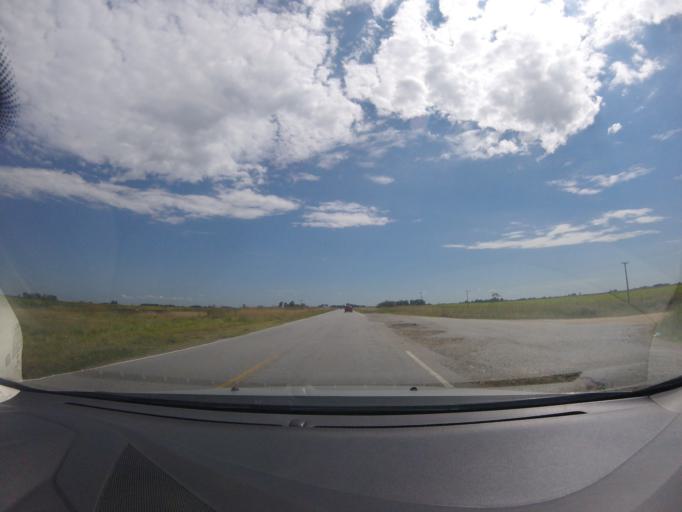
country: AR
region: Buenos Aires
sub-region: Partido de Tandil
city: Tandil
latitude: -37.2144
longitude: -59.0775
